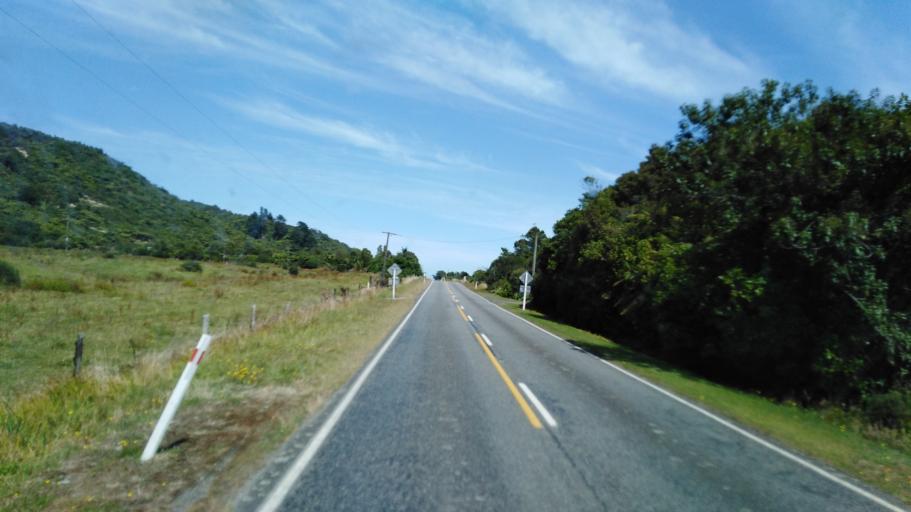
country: NZ
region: West Coast
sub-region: Buller District
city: Westport
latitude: -41.5296
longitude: 171.9435
